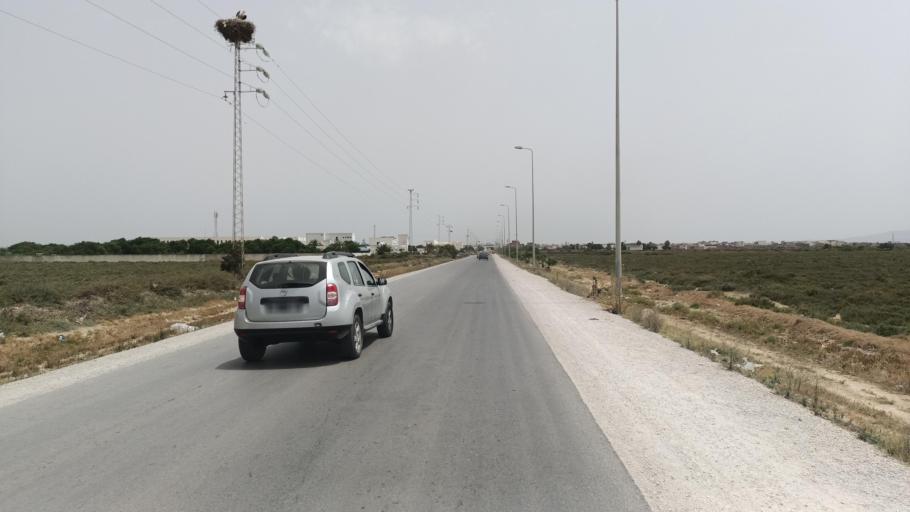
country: TN
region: Nabul
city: Manzil Bu Zalafah
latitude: 36.7148
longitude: 10.4791
